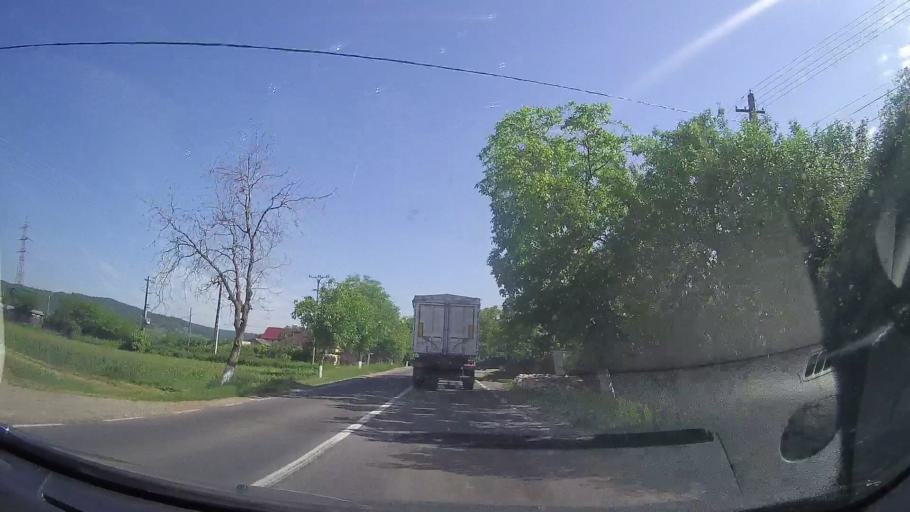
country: RO
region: Prahova
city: Drajna de Jos
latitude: 45.2355
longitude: 26.0291
